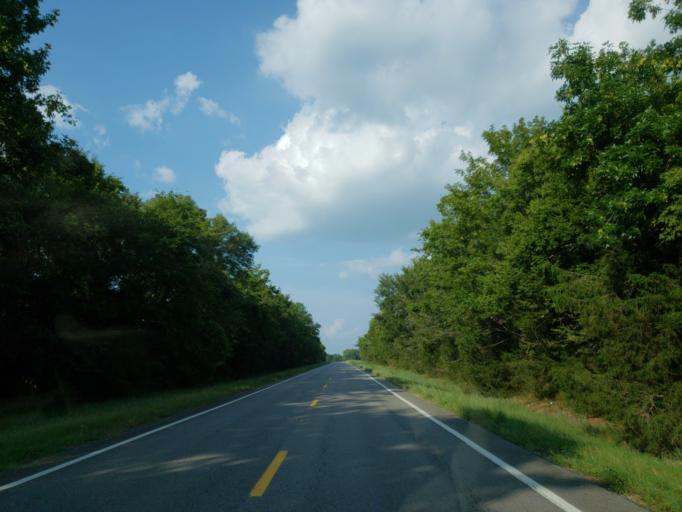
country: US
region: Alabama
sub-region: Greene County
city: Eutaw
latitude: 32.7779
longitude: -87.9842
